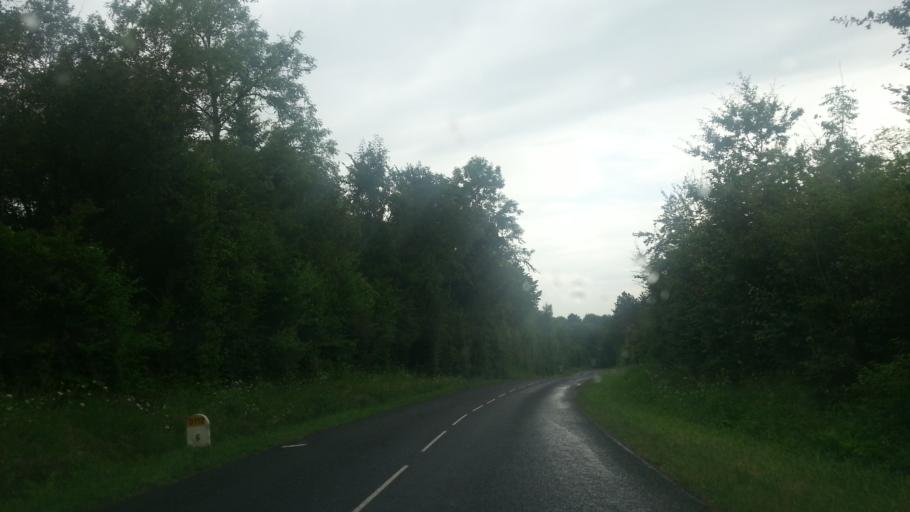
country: FR
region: Lorraine
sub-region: Departement de la Meuse
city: Verdun
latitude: 49.1925
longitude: 5.4382
